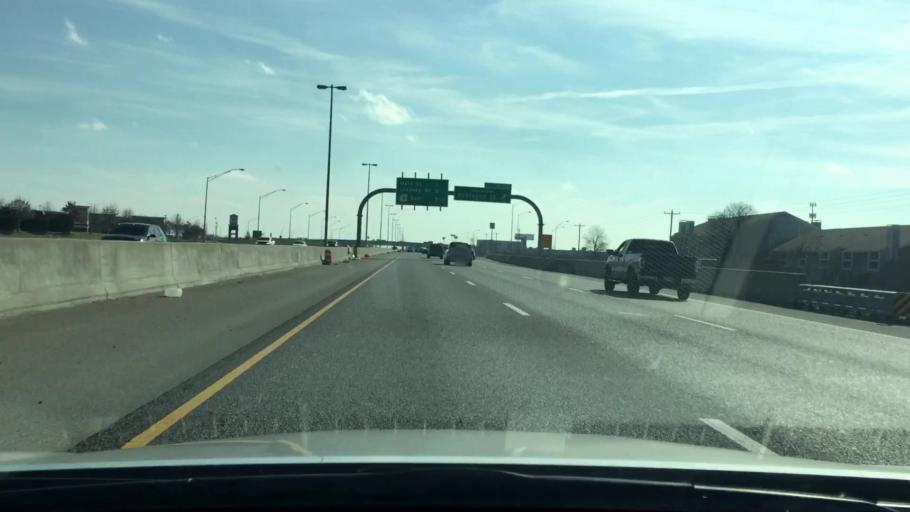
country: US
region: Oklahoma
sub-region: Cleveland County
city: Norman
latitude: 35.2395
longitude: -97.4856
